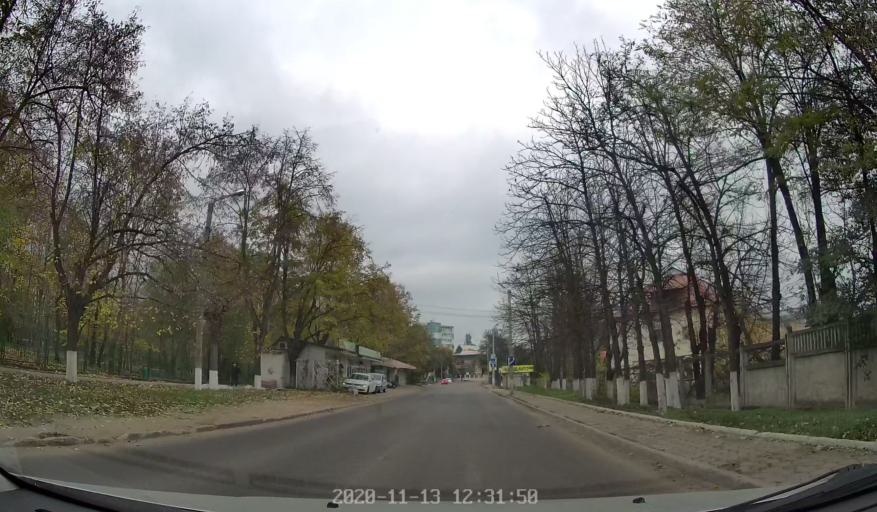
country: MD
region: Chisinau
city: Chisinau
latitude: 46.9808
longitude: 28.8371
